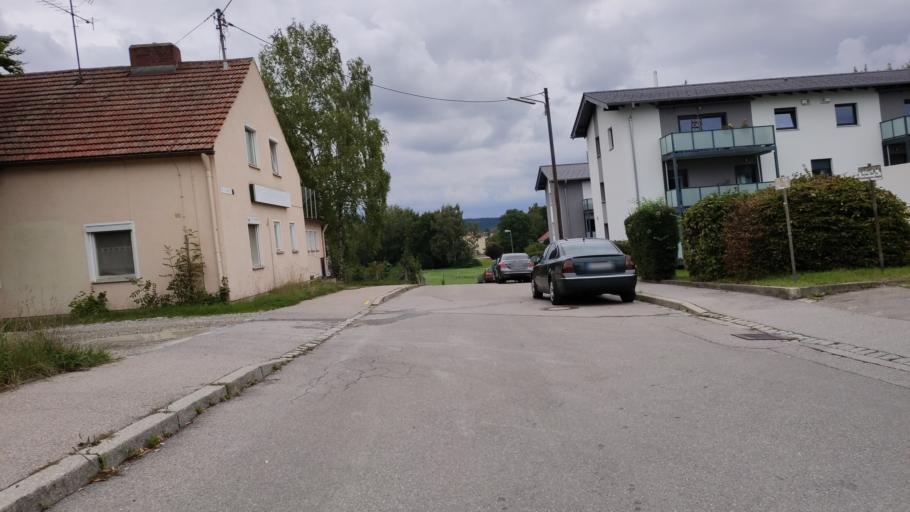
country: DE
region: Bavaria
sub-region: Swabia
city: Bobingen
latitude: 48.2620
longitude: 10.8204
